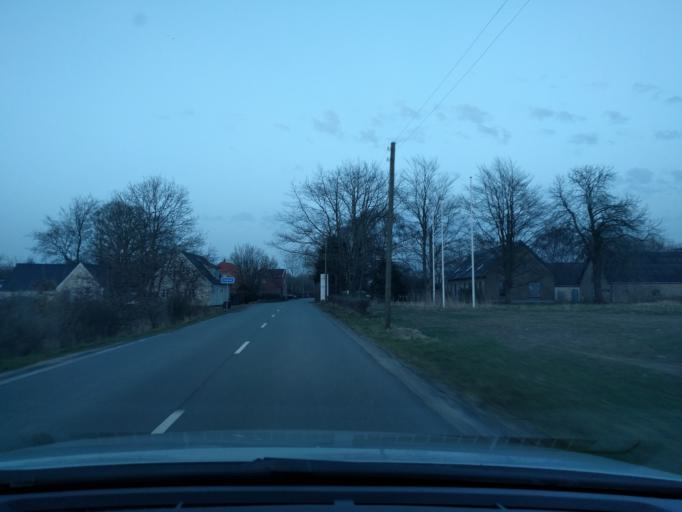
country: DK
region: South Denmark
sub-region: Odense Kommune
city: Bellinge
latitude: 55.3567
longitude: 10.3079
